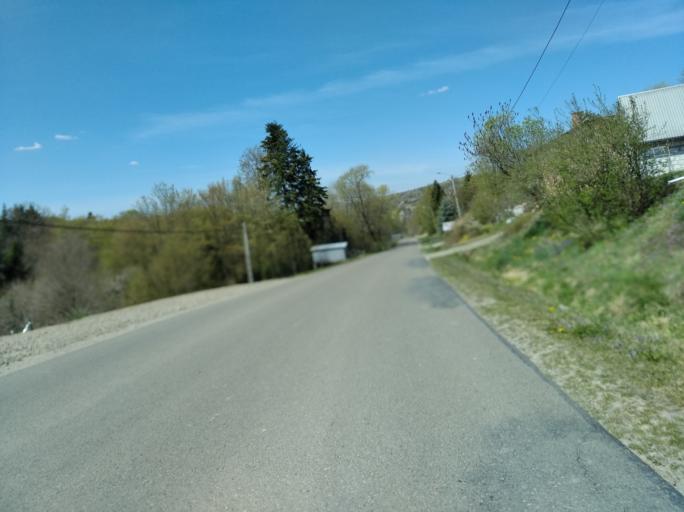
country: PL
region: Subcarpathian Voivodeship
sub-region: Powiat brzozowski
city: Golcowa
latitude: 49.7616
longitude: 22.0562
